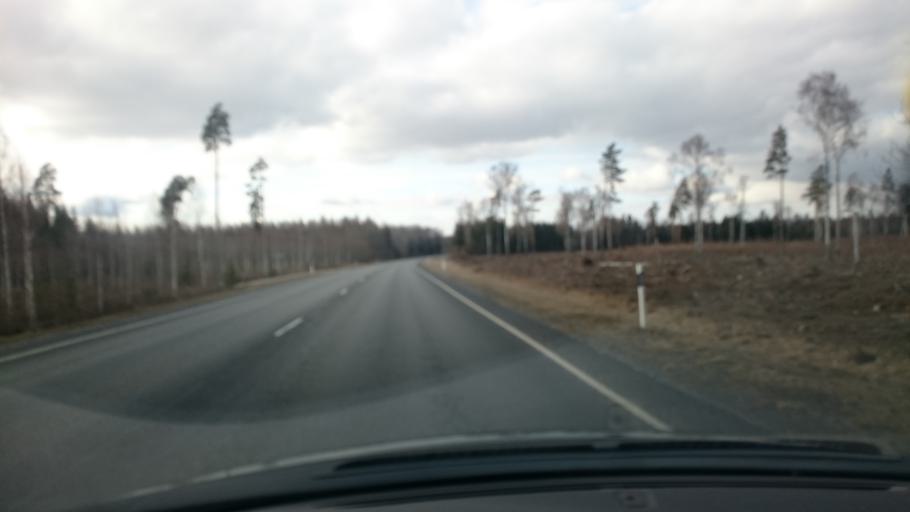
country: EE
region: Harju
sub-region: Nissi vald
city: Turba
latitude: 58.9699
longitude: 24.0647
